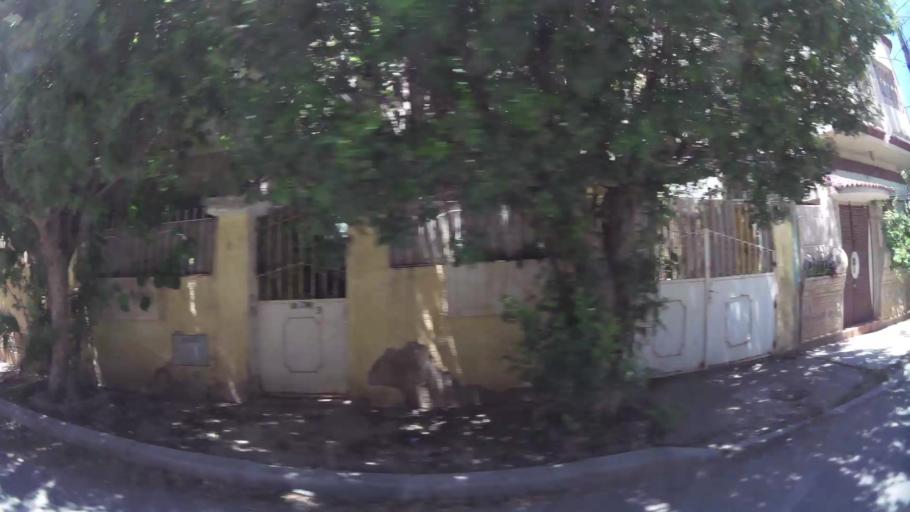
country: MA
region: Oriental
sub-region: Berkane-Taourirt
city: Madagh
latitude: 35.0842
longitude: -2.2306
